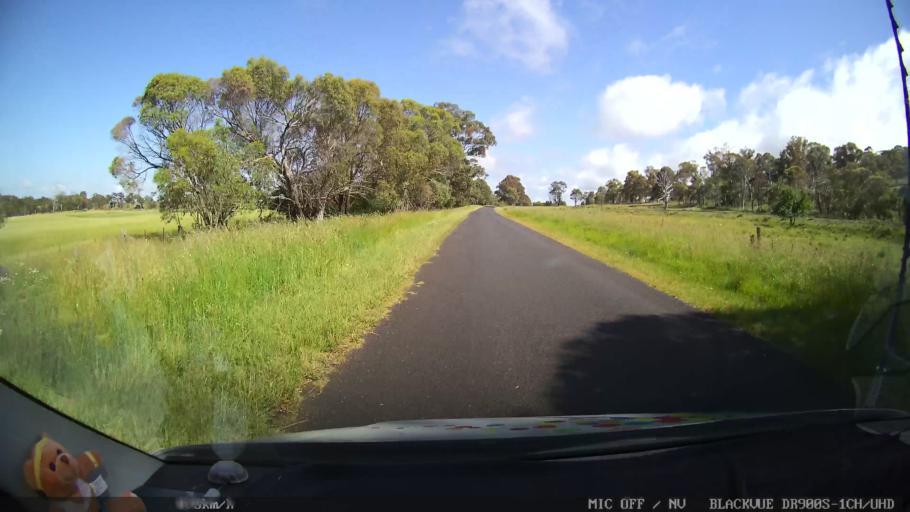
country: AU
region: New South Wales
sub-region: Guyra
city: Guyra
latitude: -30.0312
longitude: 151.6637
